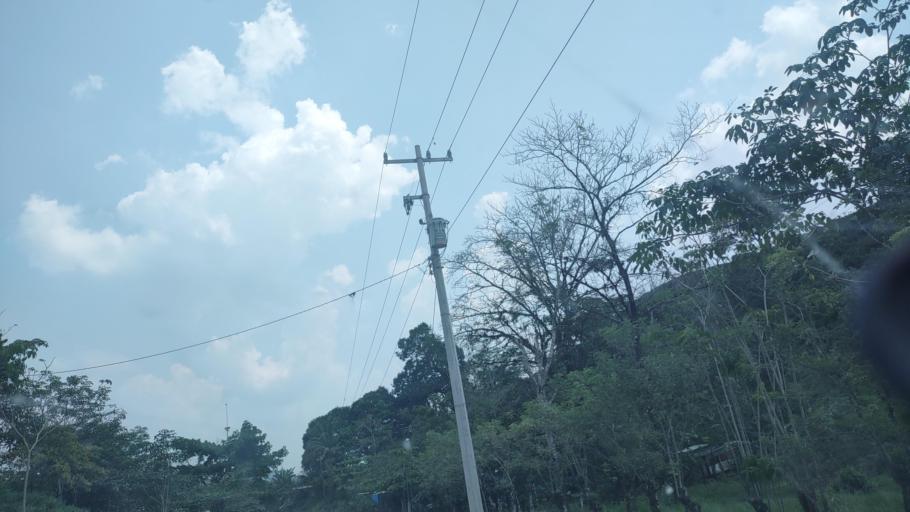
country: MX
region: Tabasco
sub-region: Huimanguillo
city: Francisco Rueda
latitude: 17.5944
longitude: -93.8982
